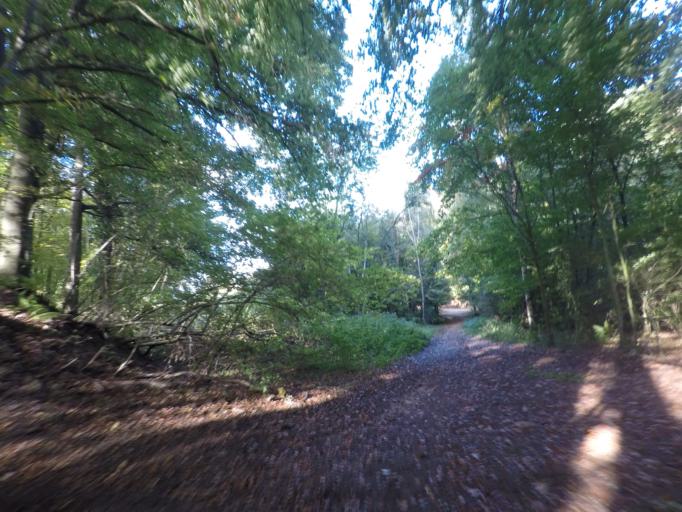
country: LU
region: Luxembourg
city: Itzig
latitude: 49.5937
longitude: 6.1738
